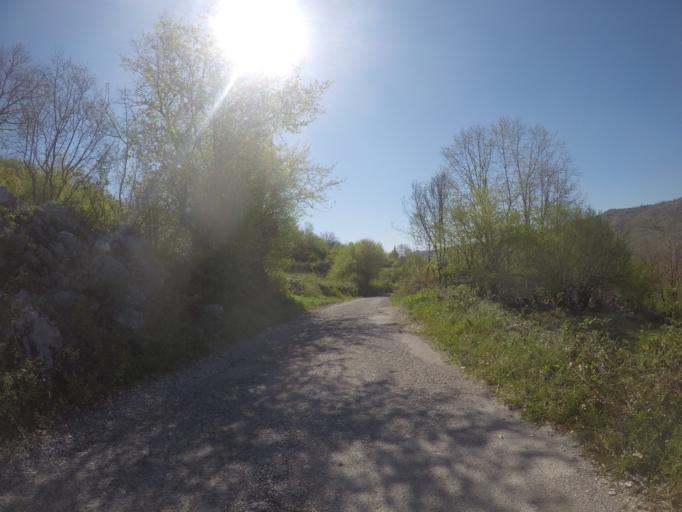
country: ME
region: Danilovgrad
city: Danilovgrad
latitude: 42.5235
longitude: 19.0494
